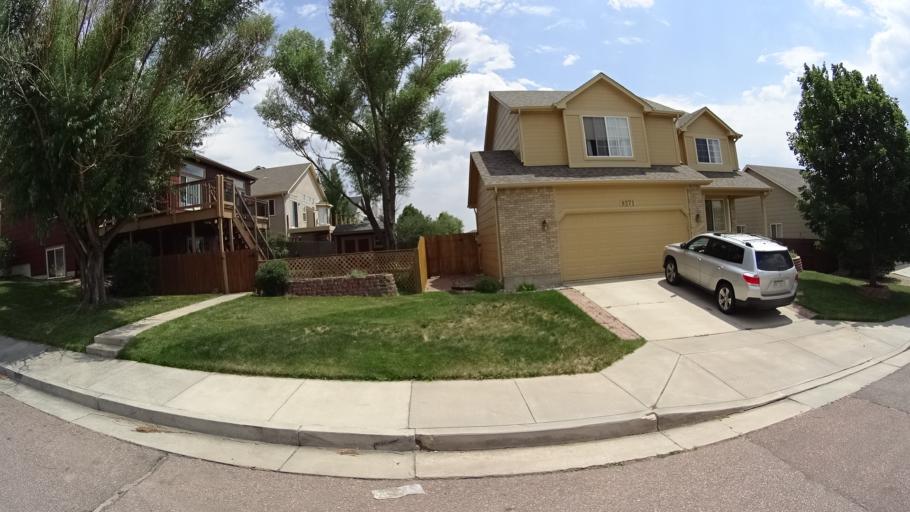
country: US
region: Colorado
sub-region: El Paso County
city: Black Forest
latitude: 38.9654
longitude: -104.7416
